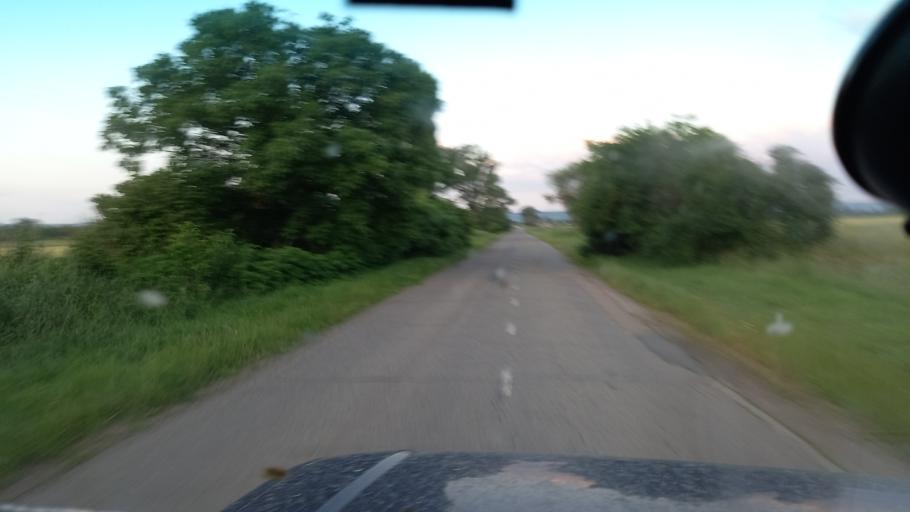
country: RU
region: Krasnodarskiy
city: Mostovskoy
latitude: 44.4231
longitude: 40.7522
